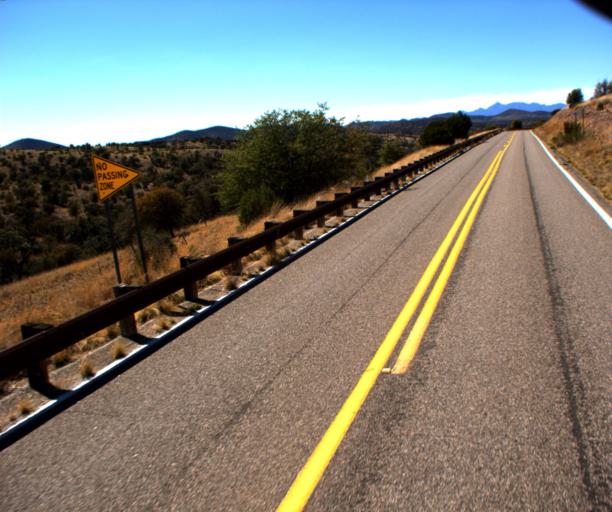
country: US
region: Arizona
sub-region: Cochise County
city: Sierra Vista
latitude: 31.4895
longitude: -110.4875
